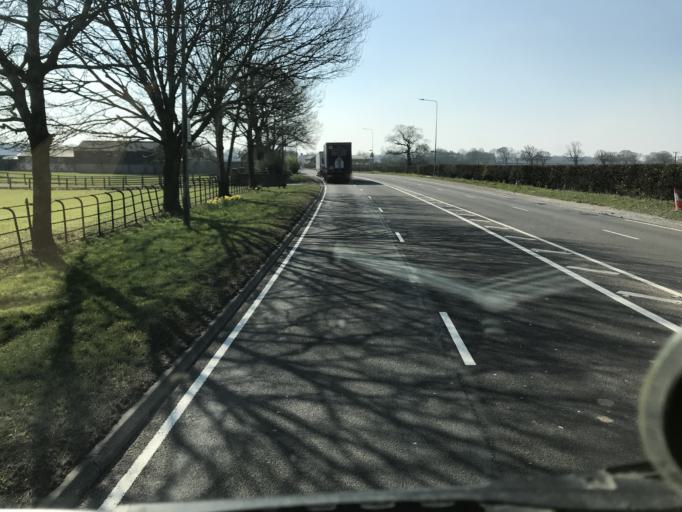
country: GB
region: England
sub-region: Cheshire East
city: Mere
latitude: 53.3094
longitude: -2.4179
